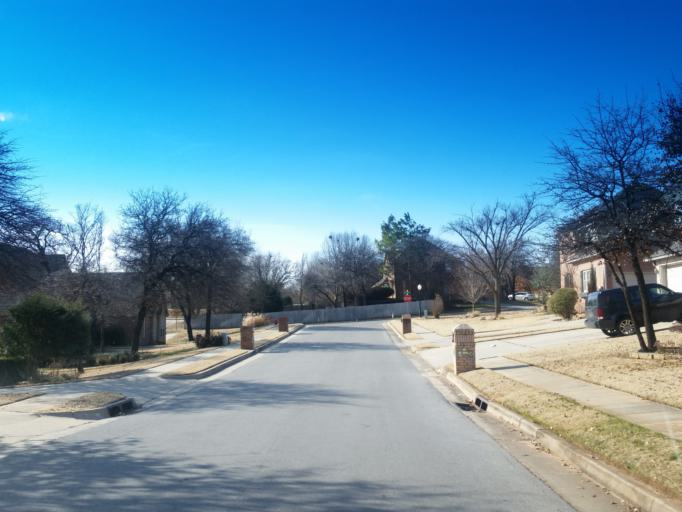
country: US
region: Oklahoma
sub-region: Oklahoma County
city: Edmond
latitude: 35.6466
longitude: -97.4286
